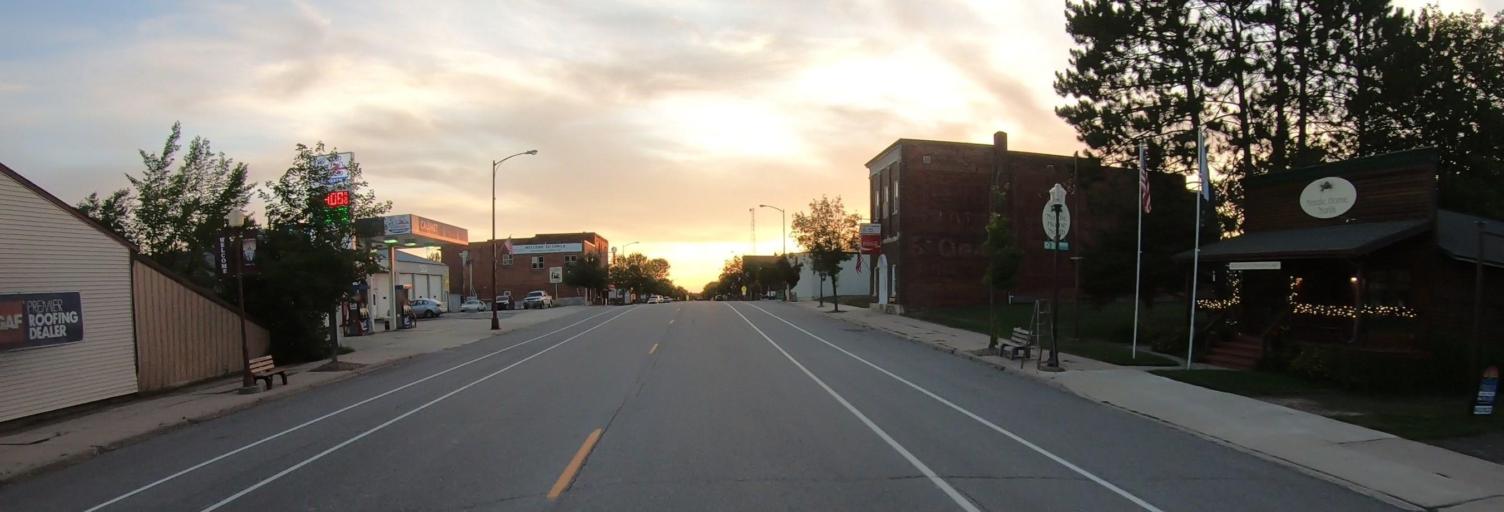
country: US
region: Minnesota
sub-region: Saint Louis County
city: Aurora
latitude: 47.8052
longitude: -92.2706
